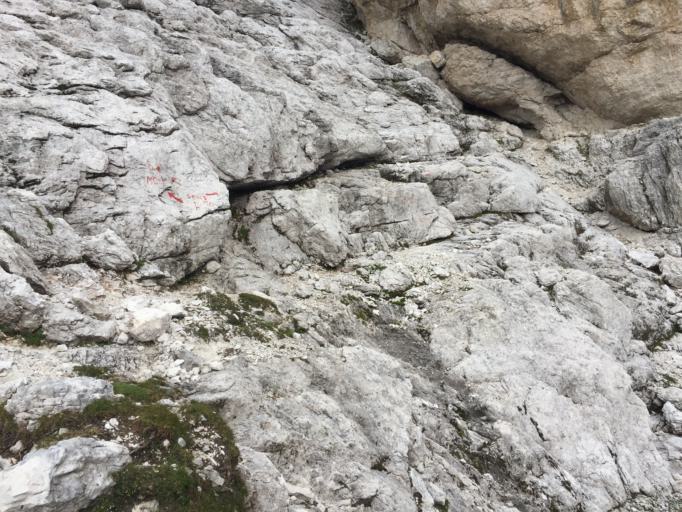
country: IT
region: Friuli Venezia Giulia
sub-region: Provincia di Udine
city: Malborghetto
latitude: 46.4283
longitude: 13.4952
